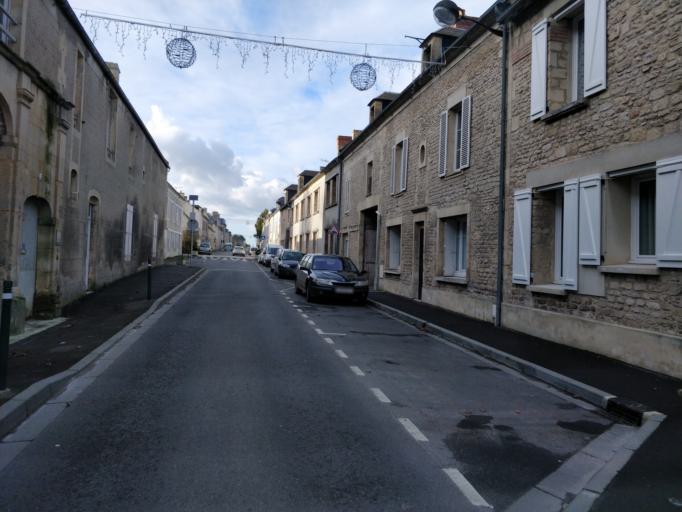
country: FR
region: Lower Normandy
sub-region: Departement du Calvados
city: Saint-Manvieu
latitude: 49.2121
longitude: -0.5176
